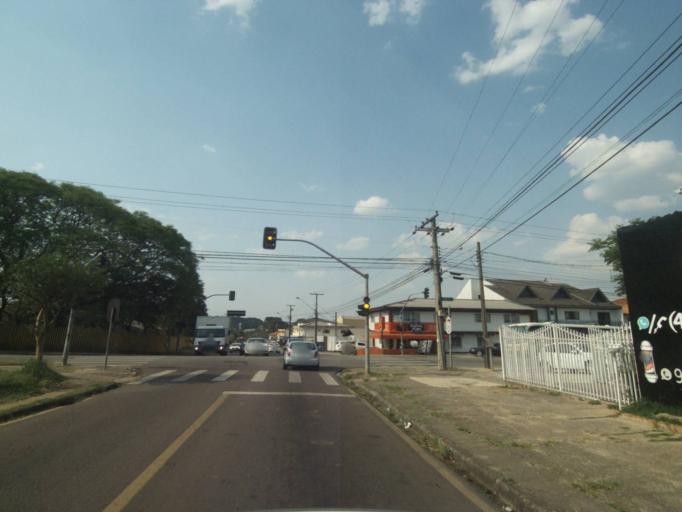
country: BR
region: Parana
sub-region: Sao Jose Dos Pinhais
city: Sao Jose dos Pinhais
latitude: -25.5320
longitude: -49.2423
